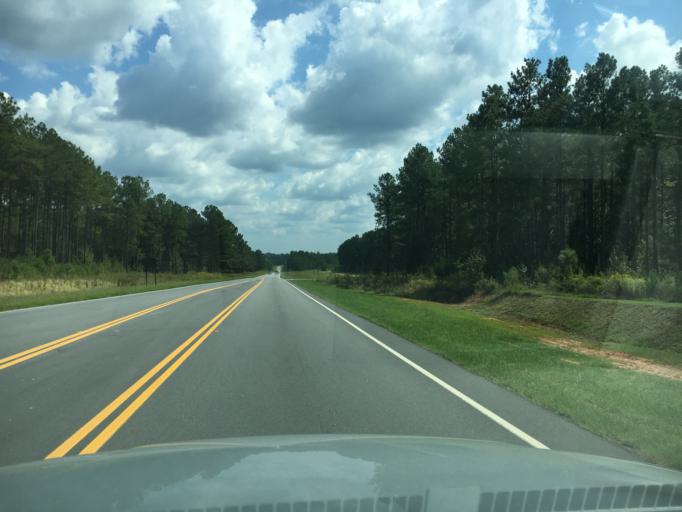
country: US
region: South Carolina
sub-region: Greenwood County
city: Greenwood
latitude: 34.1571
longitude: -82.1733
